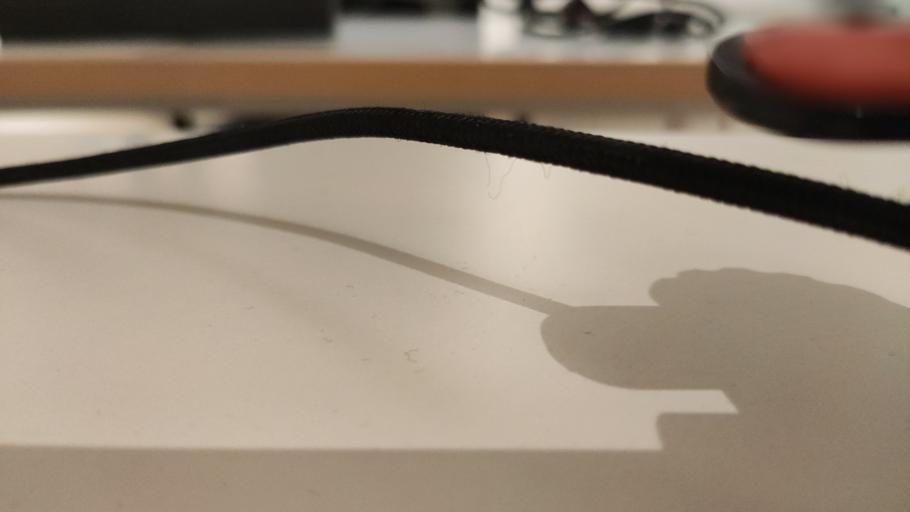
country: RU
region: Moskovskaya
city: Dorokhovo
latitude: 55.4260
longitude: 36.3566
